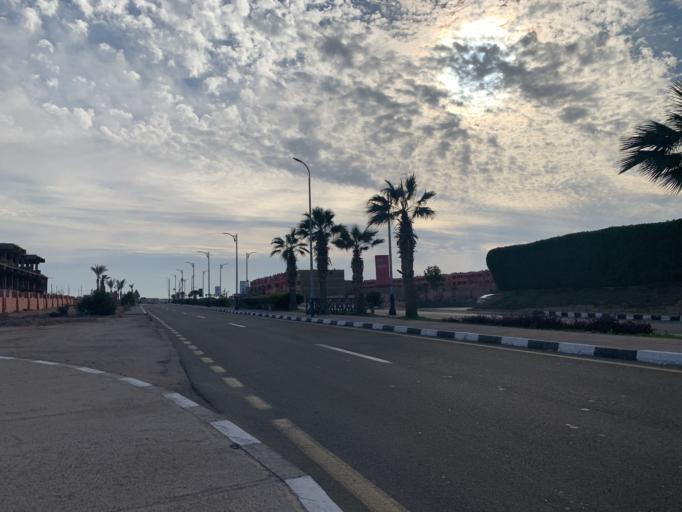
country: EG
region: South Sinai
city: Sharm el-Sheikh
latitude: 28.0178
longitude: 34.4346
